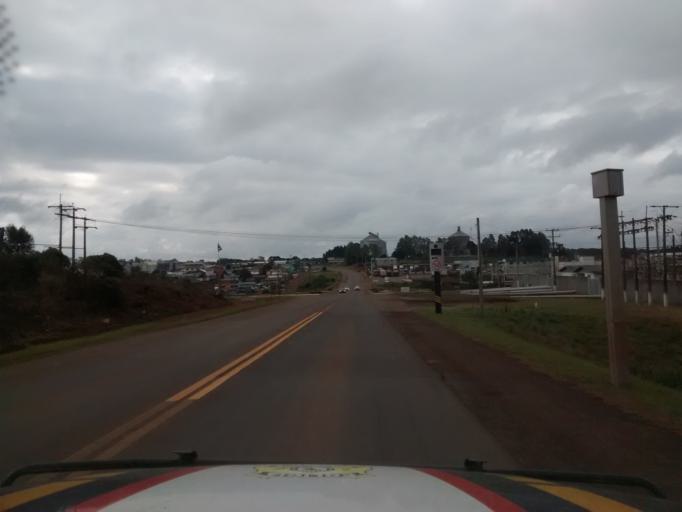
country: BR
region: Rio Grande do Sul
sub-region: Lagoa Vermelha
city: Lagoa Vermelha
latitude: -28.2168
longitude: -51.5099
